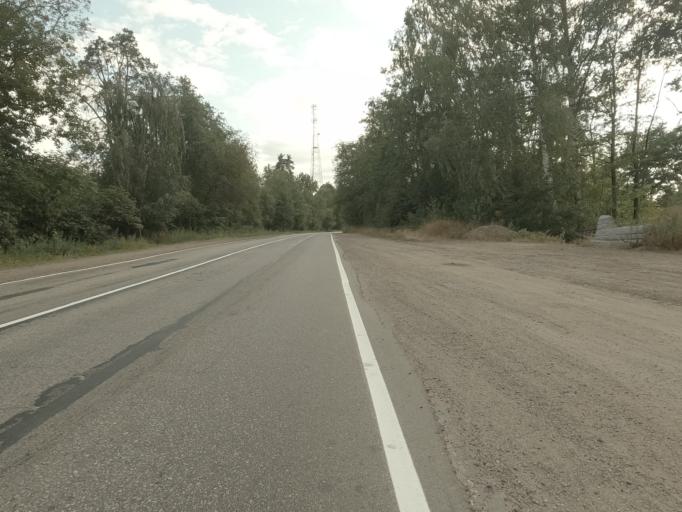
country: RU
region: Leningrad
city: Lesogorskiy
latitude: 60.8609
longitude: 28.9691
